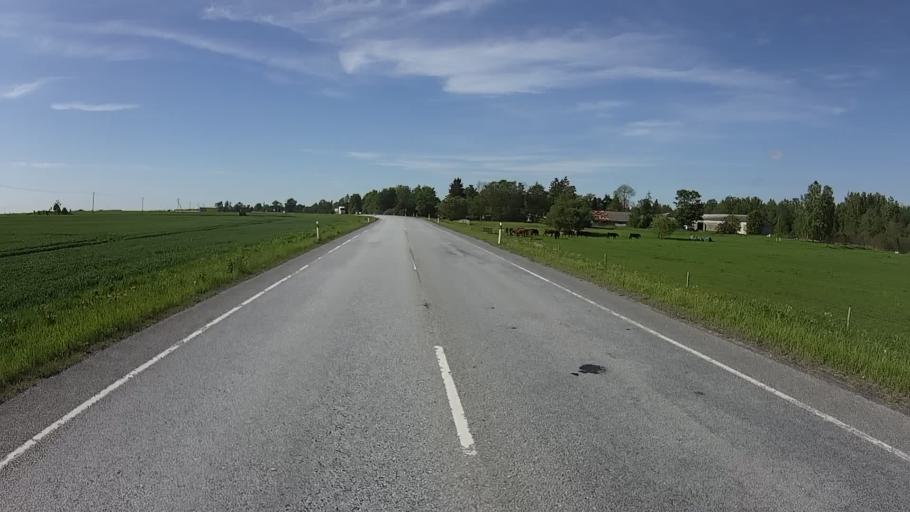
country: EE
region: Laeaene-Virumaa
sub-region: Haljala vald
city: Haljala
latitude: 59.4116
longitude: 26.2934
